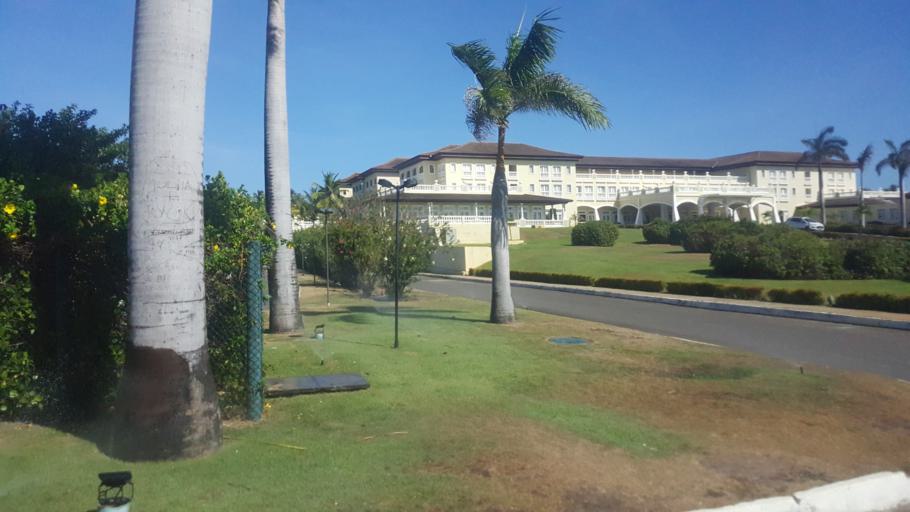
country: BR
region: Bahia
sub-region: Mata De Sao Joao
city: Mata de Sao Joao
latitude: -12.4423
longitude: -37.9242
